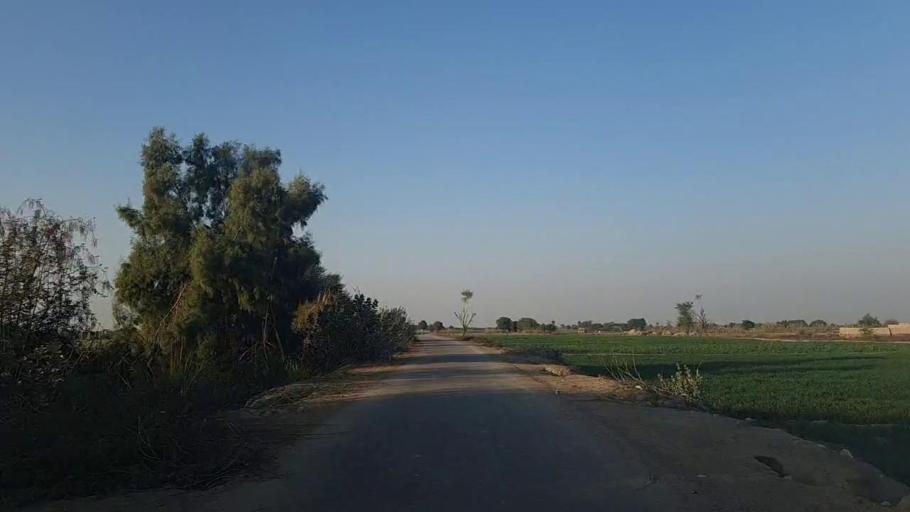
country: PK
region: Sindh
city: Jam Sahib
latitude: 26.3468
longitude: 68.6734
